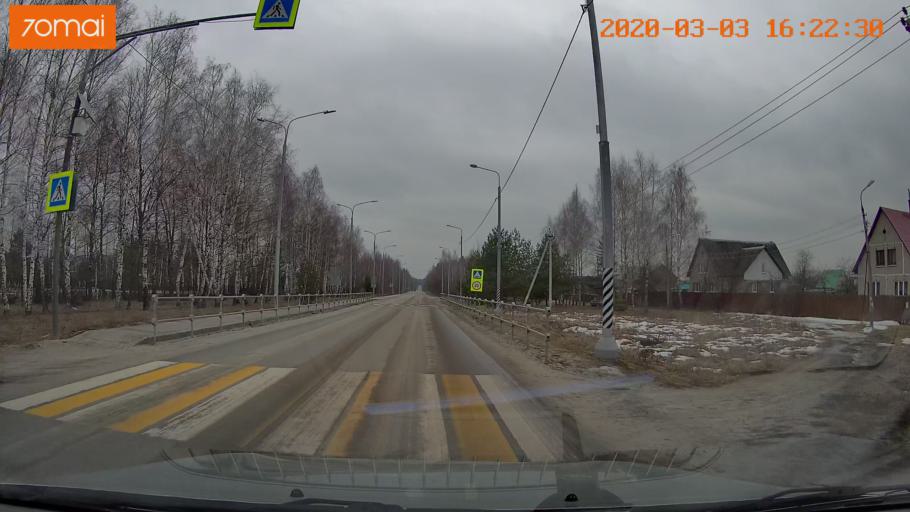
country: RU
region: Moskovskaya
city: Imeni Tsyurupy
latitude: 55.4913
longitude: 38.6482
